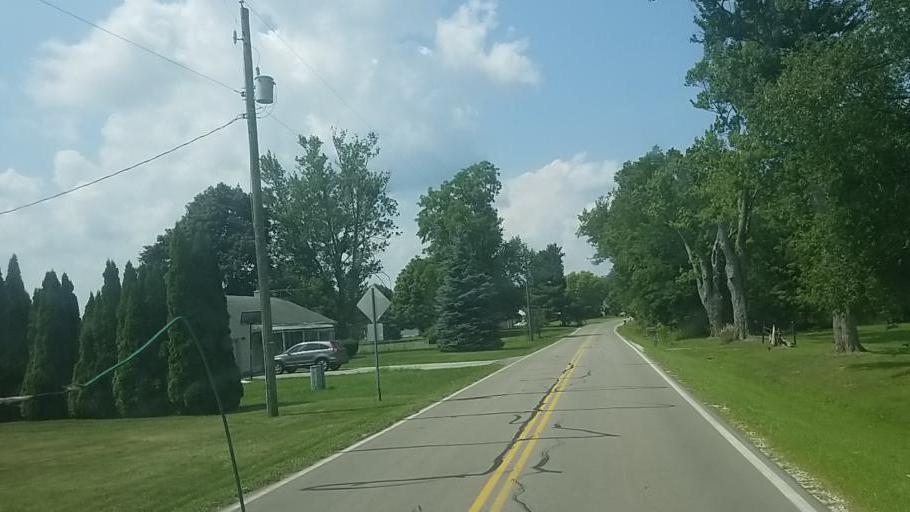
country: US
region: Ohio
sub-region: Crawford County
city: Crestline
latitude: 40.7988
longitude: -82.7762
